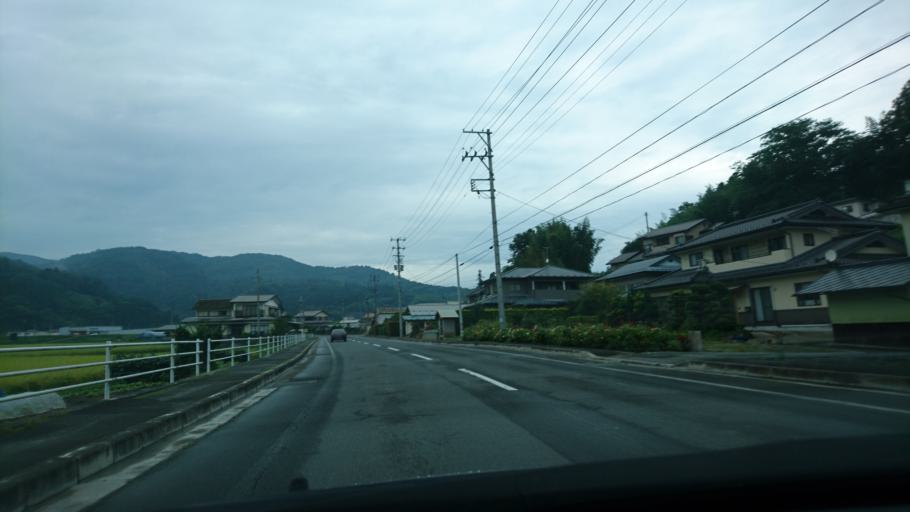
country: JP
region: Iwate
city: Ichinoseki
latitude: 38.9743
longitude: 141.2431
